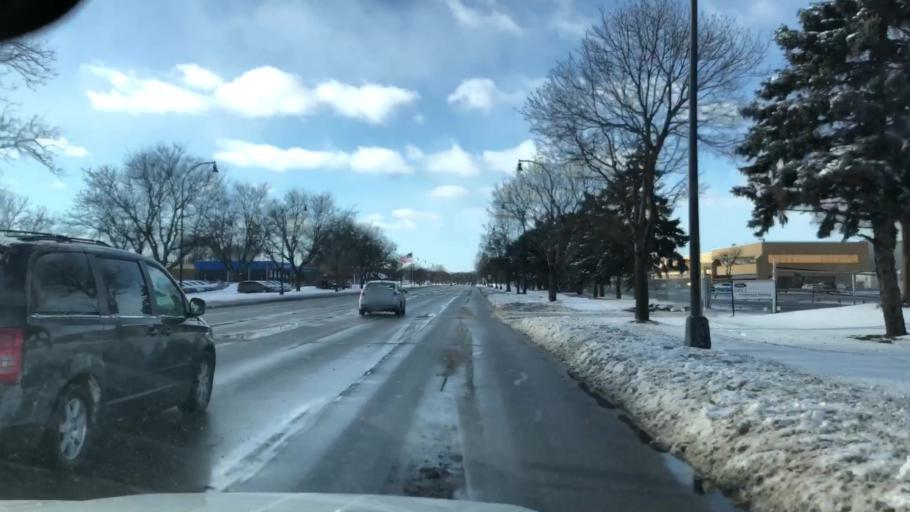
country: US
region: Michigan
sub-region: Wayne County
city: Livonia
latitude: 42.3680
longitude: -83.3933
